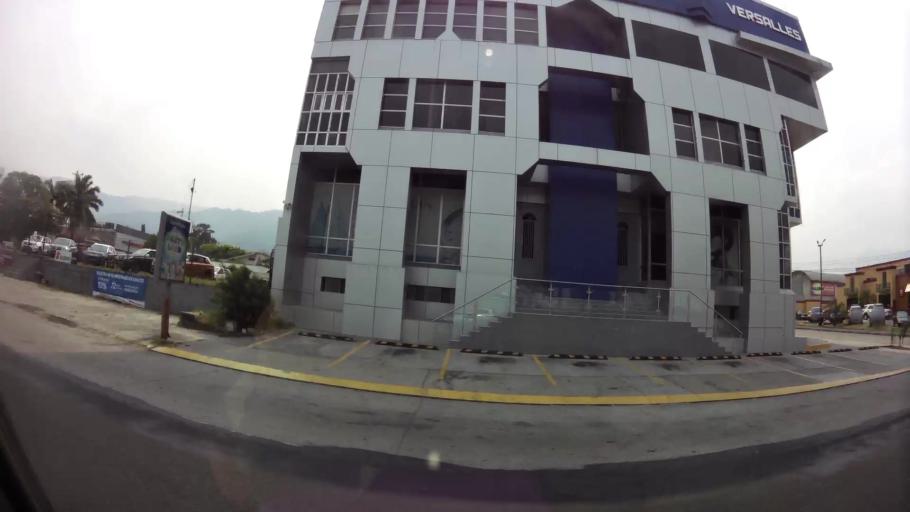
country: HN
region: Cortes
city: Armenta
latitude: 15.5014
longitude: -88.0380
